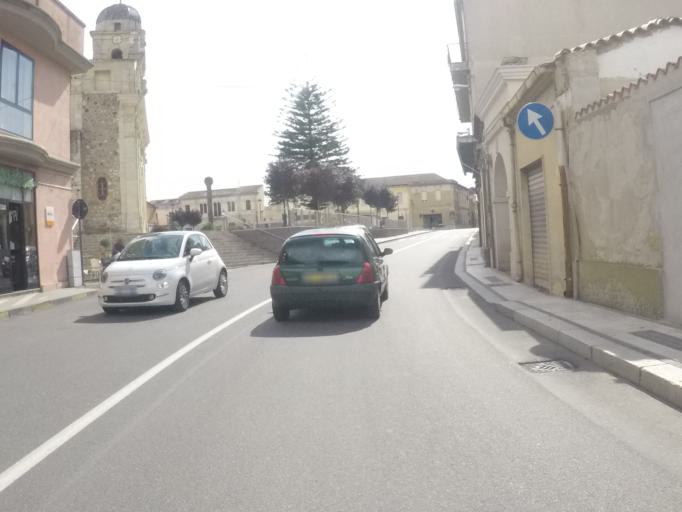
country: IT
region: Sardinia
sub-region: Provincia di Oristano
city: Terralba
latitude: 39.7209
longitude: 8.6373
